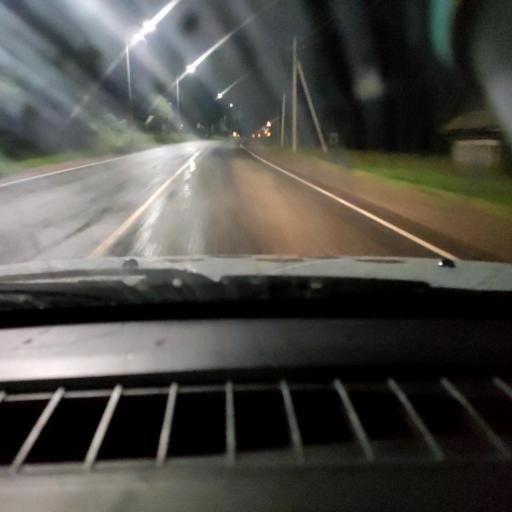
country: RU
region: Udmurtiya
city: Igra
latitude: 57.3297
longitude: 53.1653
